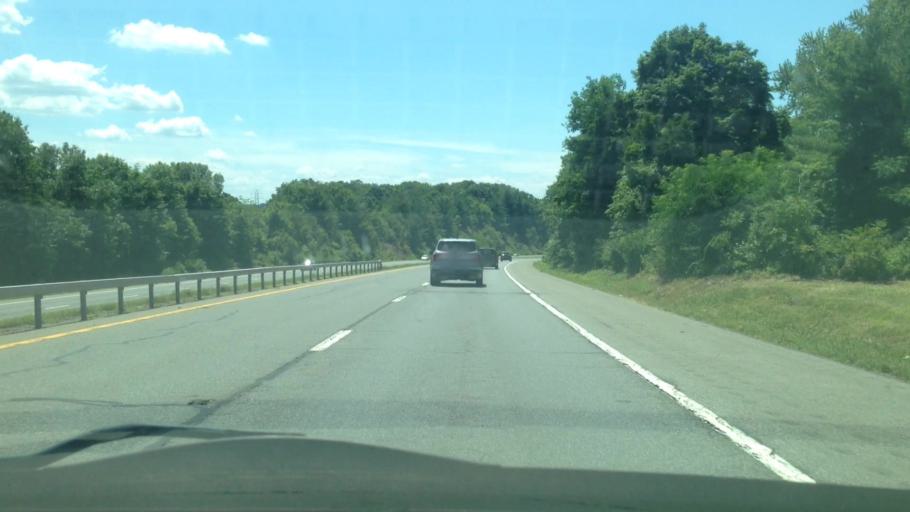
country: US
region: New York
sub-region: Ulster County
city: Lincoln Park
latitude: 41.9568
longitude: -74.0261
